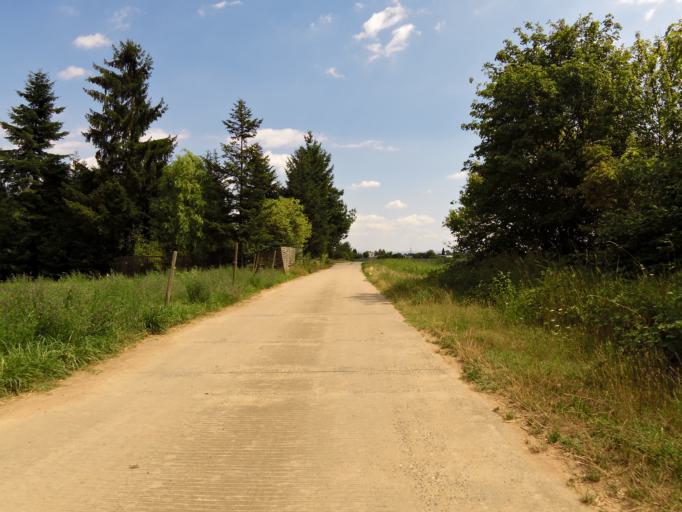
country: DE
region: Rheinland-Pfalz
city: Fussgonheim
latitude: 49.4530
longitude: 8.2834
